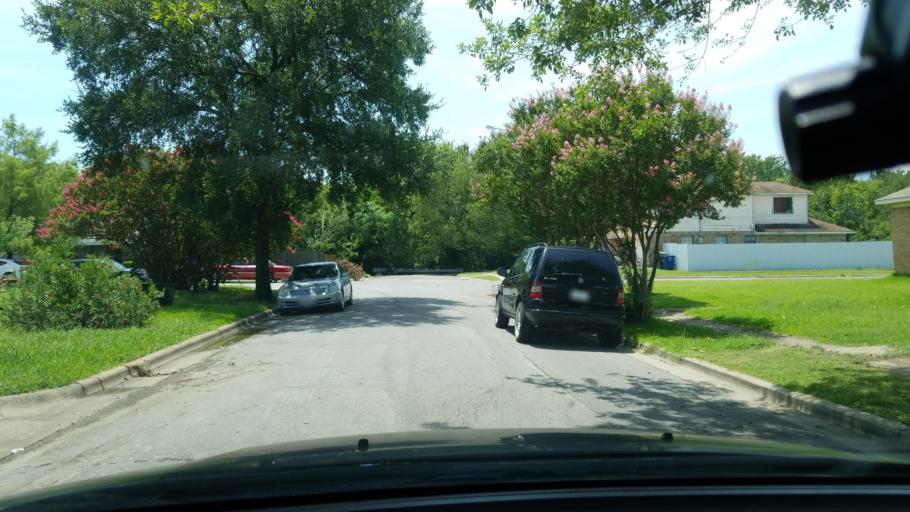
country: US
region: Texas
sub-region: Dallas County
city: Balch Springs
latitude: 32.7386
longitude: -96.6521
